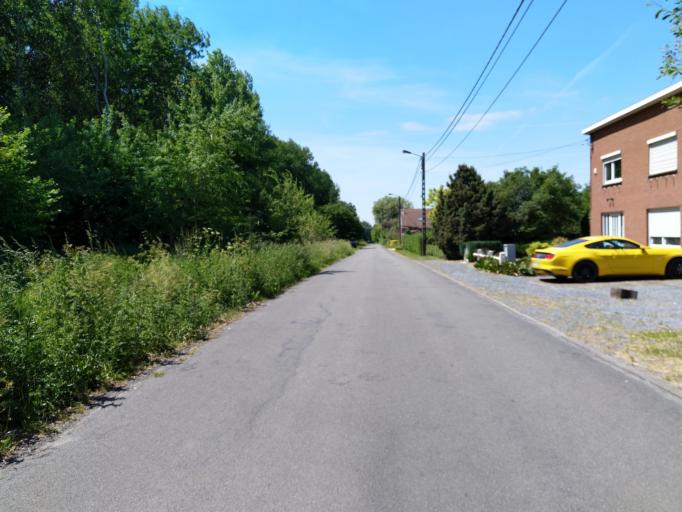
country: BE
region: Wallonia
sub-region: Province du Hainaut
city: Saint-Ghislain
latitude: 50.5088
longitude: 3.8390
